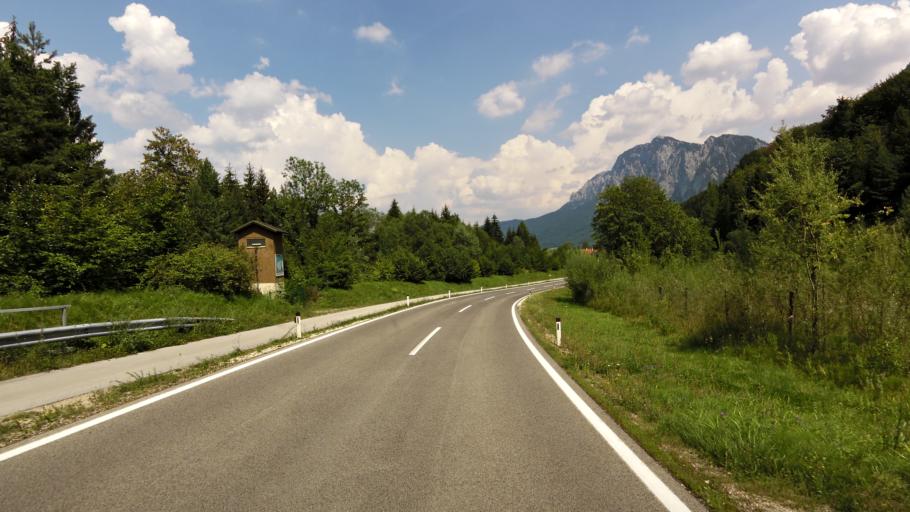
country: AT
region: Upper Austria
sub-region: Politischer Bezirk Vocklabruck
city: Steinbach am Attersee
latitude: 47.7942
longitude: 13.5124
